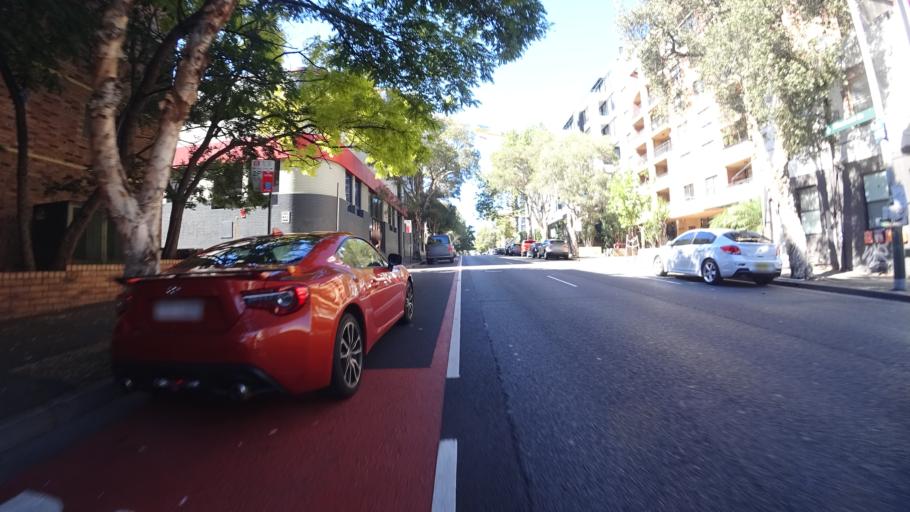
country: AU
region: New South Wales
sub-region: City of Sydney
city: Redfern
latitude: -33.8877
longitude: 151.2082
